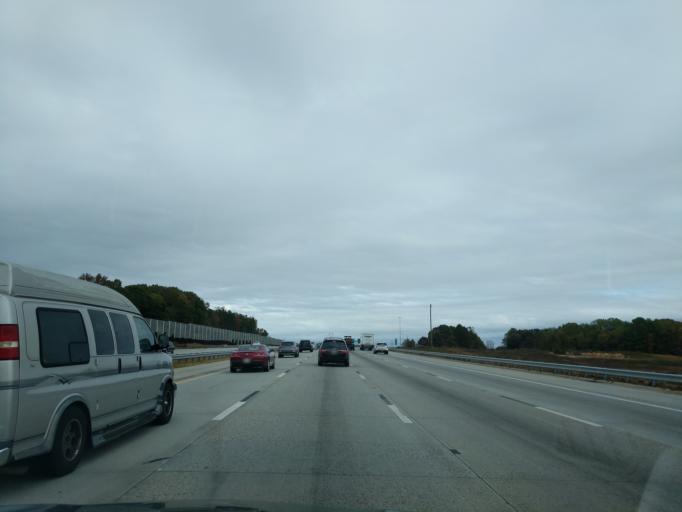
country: US
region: North Carolina
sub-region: Rowan County
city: Spencer
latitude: 35.7256
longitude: -80.3836
